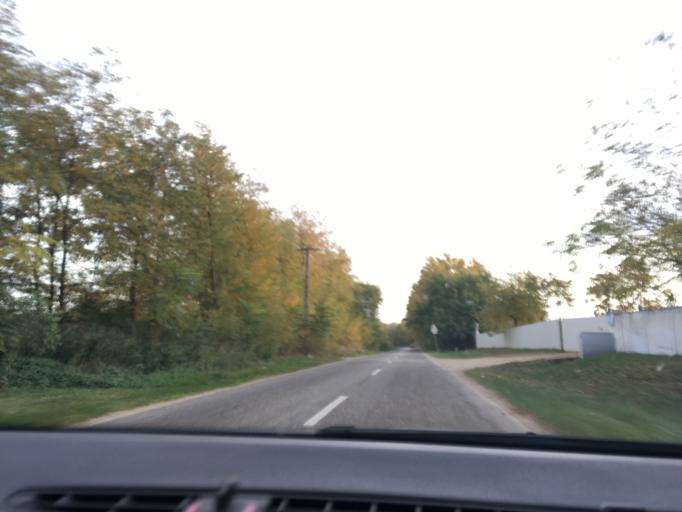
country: HU
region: Szabolcs-Szatmar-Bereg
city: Mariapocs
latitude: 47.8623
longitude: 22.0302
